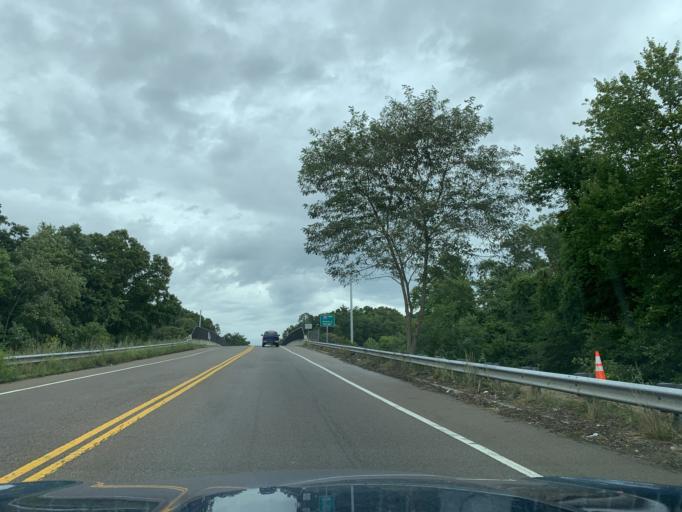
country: US
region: Rhode Island
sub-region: Bristol County
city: Warren
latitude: 41.7732
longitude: -71.2623
